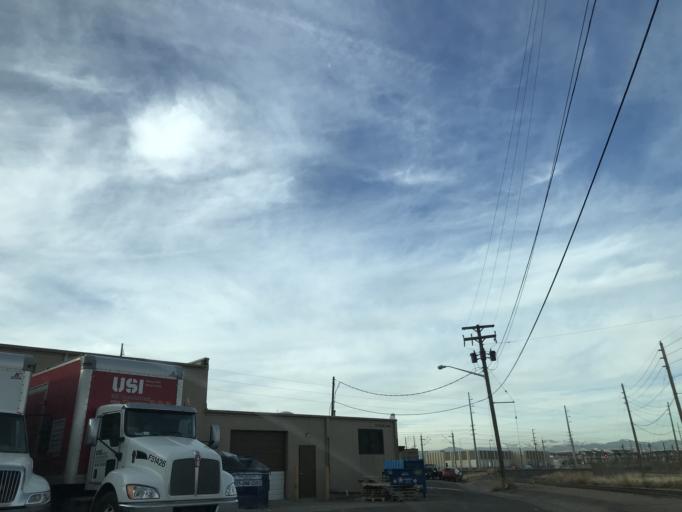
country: US
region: Colorado
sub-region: Adams County
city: Commerce City
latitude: 39.7764
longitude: -104.9276
